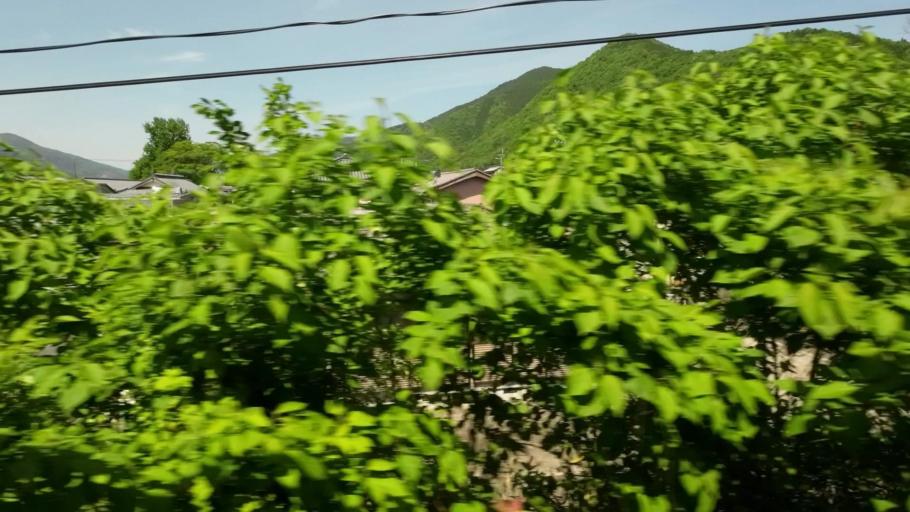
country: JP
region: Tokushima
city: Ikedacho
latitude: 34.0419
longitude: 133.8669
